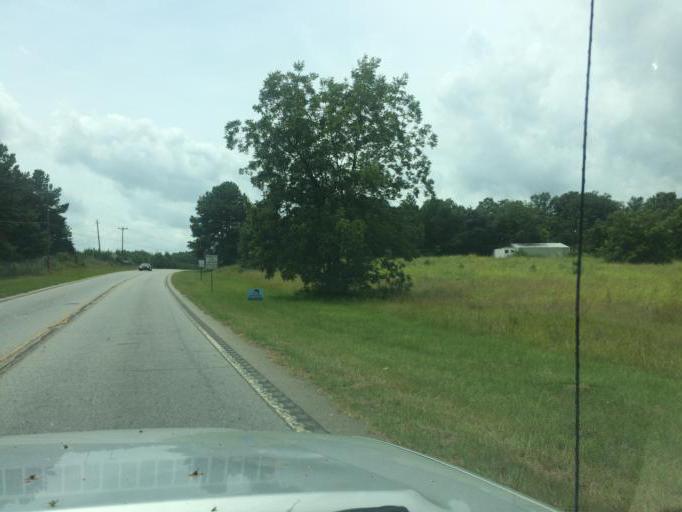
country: US
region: South Carolina
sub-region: Anderson County
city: Centerville
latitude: 34.5073
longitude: -82.7630
